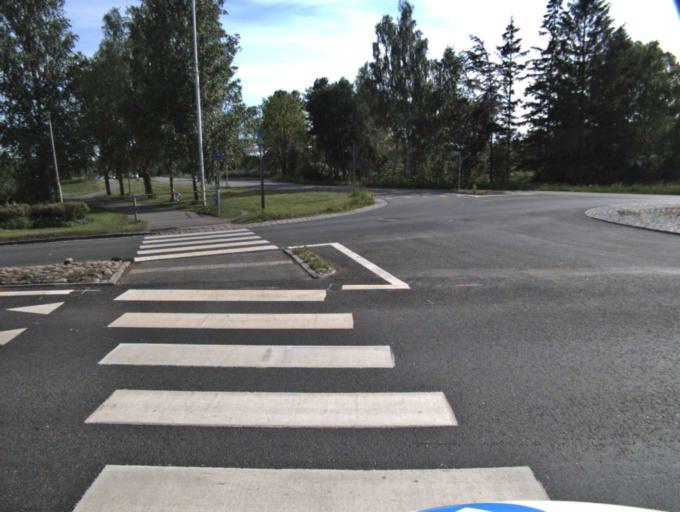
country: SE
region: Skane
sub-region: Kristianstads Kommun
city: Kristianstad
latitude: 56.0523
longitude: 14.1898
